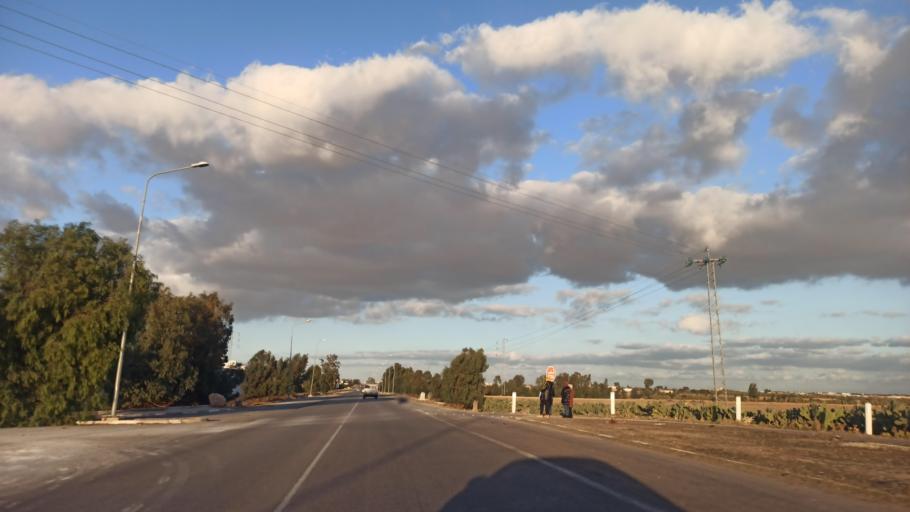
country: TN
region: Susah
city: Sidi Bou Ali
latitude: 35.9151
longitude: 10.2823
